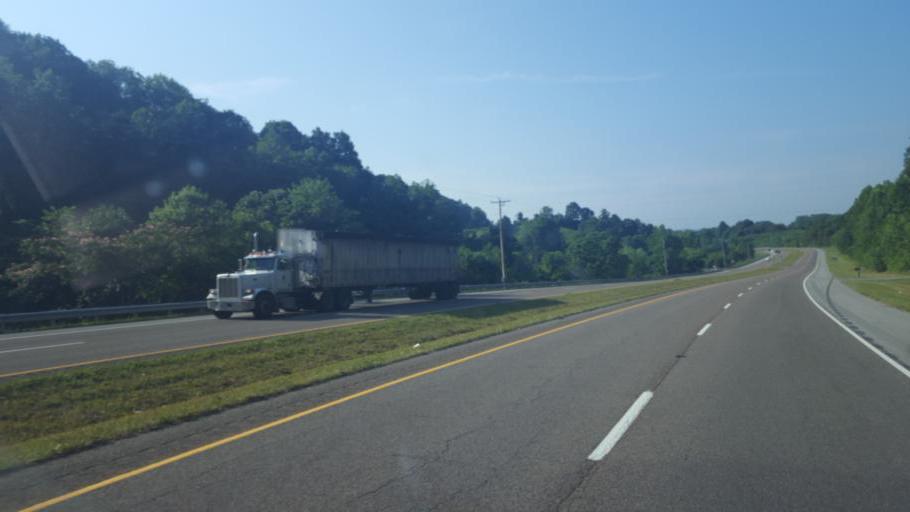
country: US
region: Tennessee
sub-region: Carter County
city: Elizabethton
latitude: 36.3925
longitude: -82.2270
